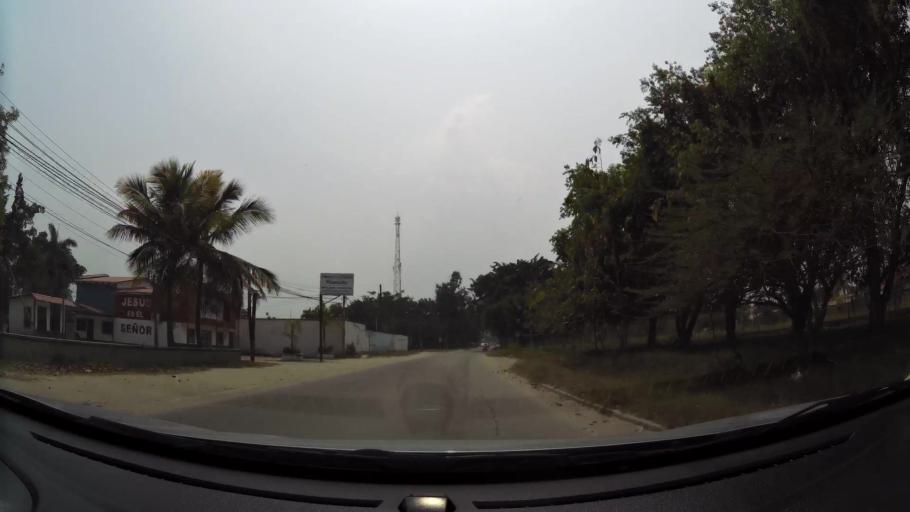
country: HN
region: Cortes
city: La Lima
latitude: 15.4363
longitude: -87.9136
